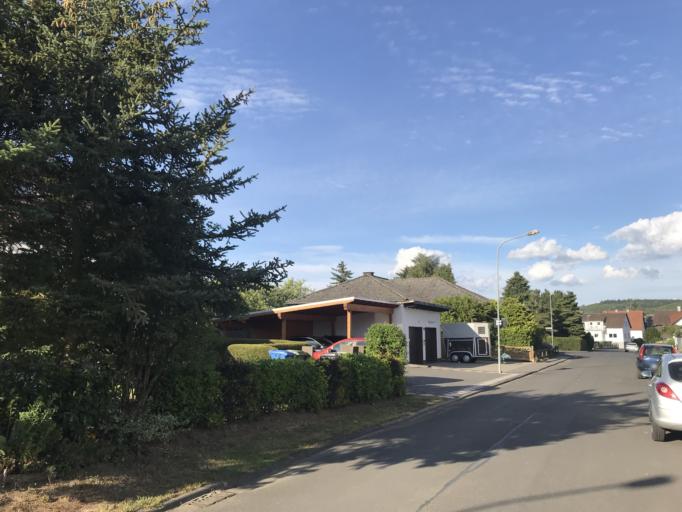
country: DE
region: Hesse
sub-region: Regierungsbezirk Giessen
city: Lohra
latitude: 50.6872
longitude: 8.6011
